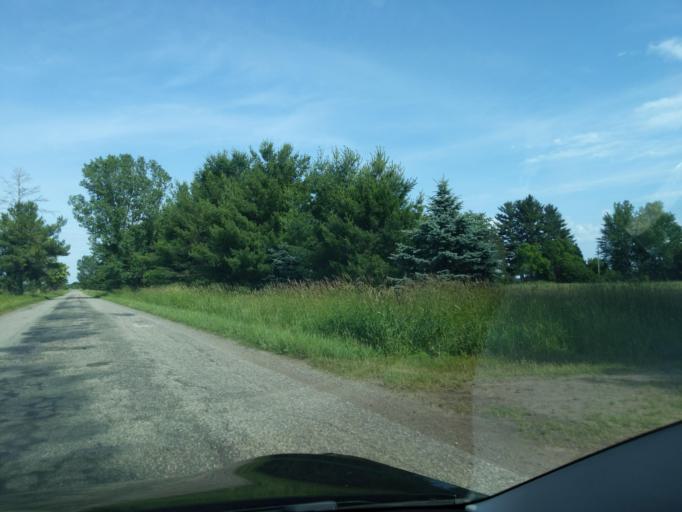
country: US
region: Michigan
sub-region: Newaygo County
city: Fremont
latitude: 43.4205
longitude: -86.0191
